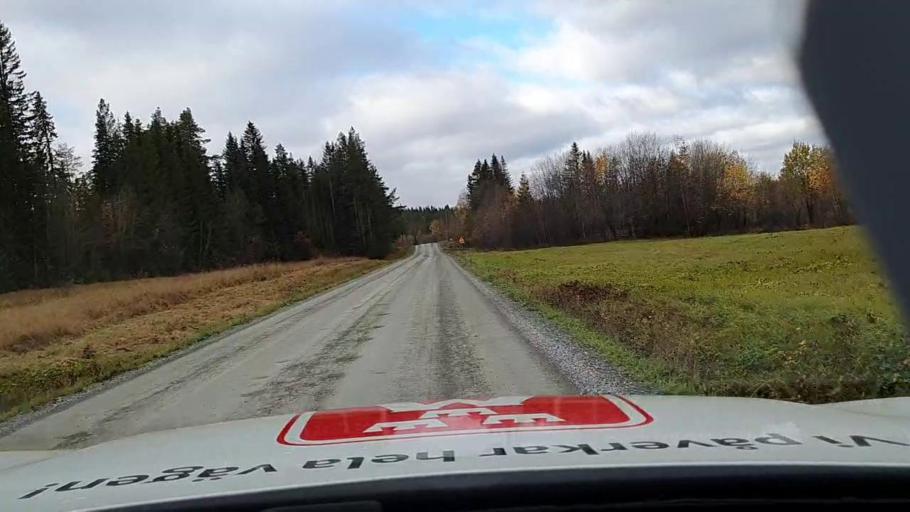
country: SE
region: Jaemtland
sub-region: Bergs Kommun
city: Hoverberg
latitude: 62.9819
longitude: 14.2050
